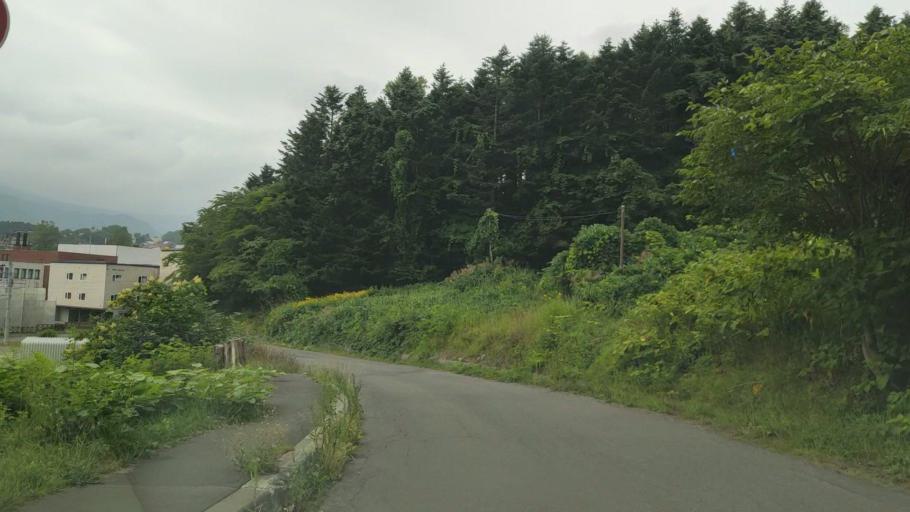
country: JP
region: Hokkaido
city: Otaru
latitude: 43.1855
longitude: 140.9932
